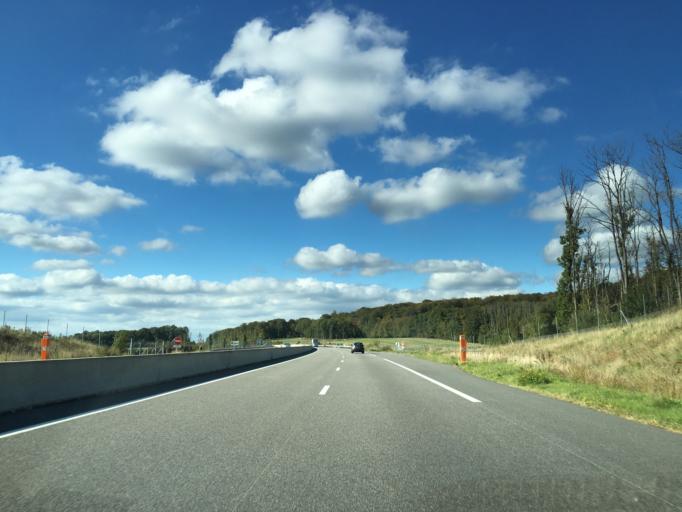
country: FR
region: Lorraine
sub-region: Departement de Meurthe-et-Moselle
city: Baccarat
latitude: 48.4987
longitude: 6.6950
